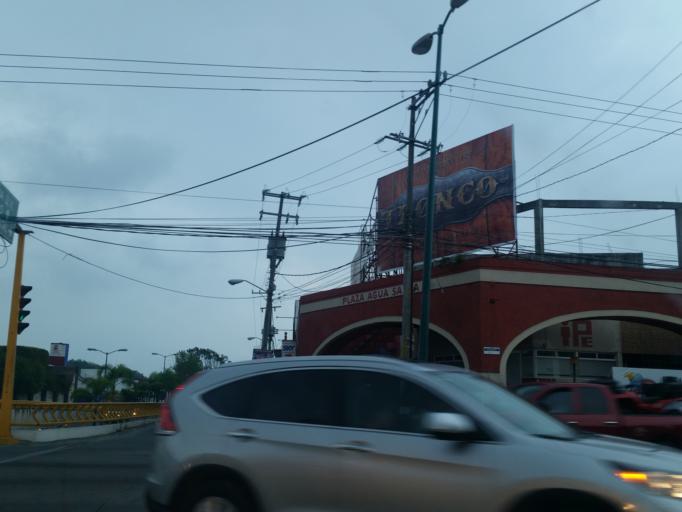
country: MX
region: Veracruz
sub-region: Xalapa
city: Xalapa de Enriquez
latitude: 19.5255
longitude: -96.9065
